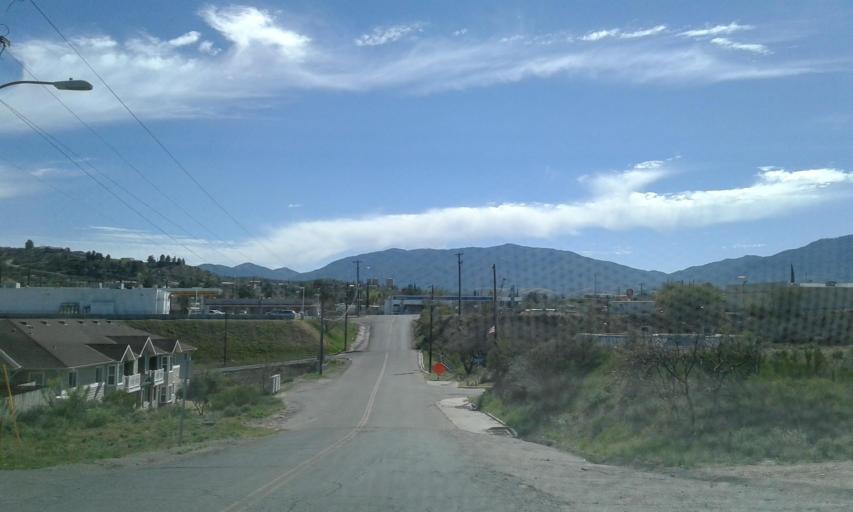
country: US
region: Arizona
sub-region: Gila County
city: Central Heights-Midland City
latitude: 33.4213
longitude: -110.8128
